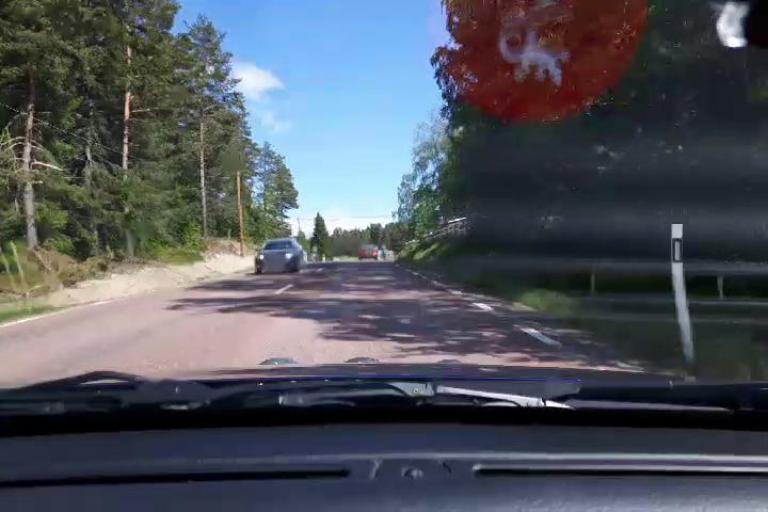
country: SE
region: Gaevleborg
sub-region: Hudiksvalls Kommun
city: Delsbo
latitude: 61.7971
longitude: 16.5164
